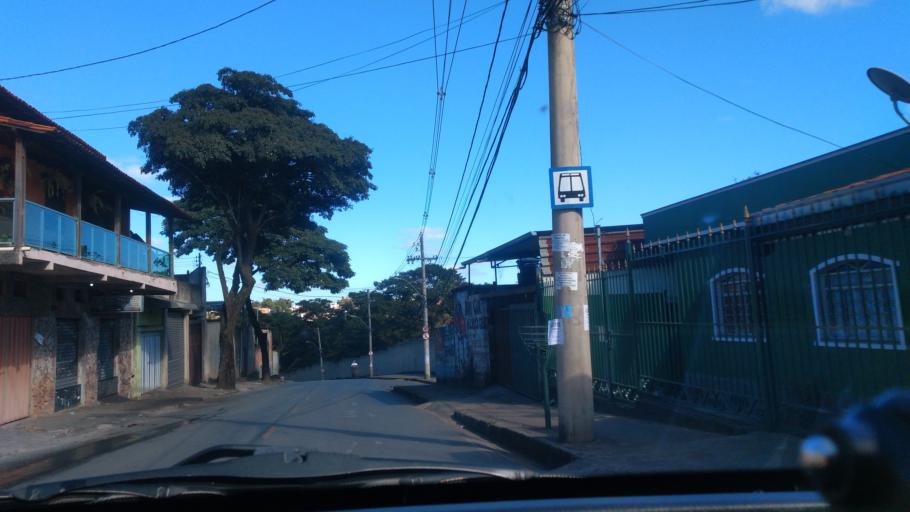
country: BR
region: Minas Gerais
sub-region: Santa Luzia
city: Santa Luzia
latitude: -19.8112
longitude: -43.9442
